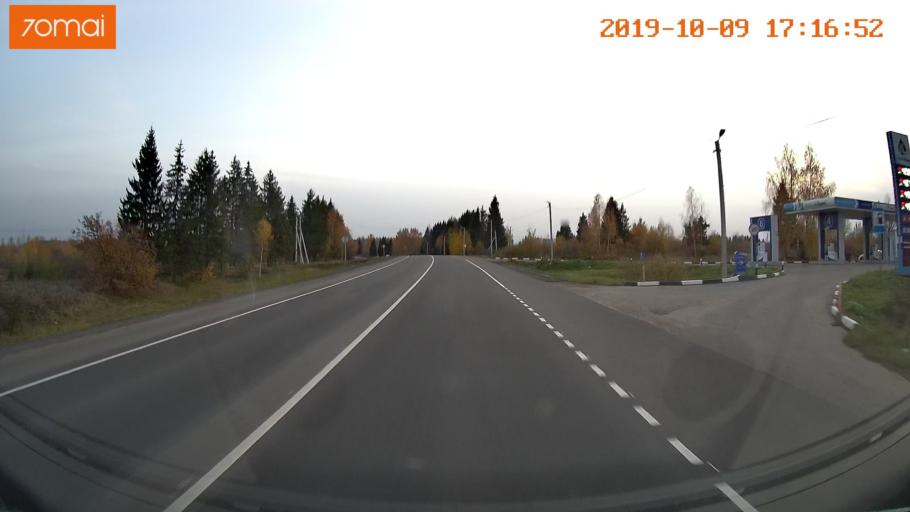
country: RU
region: Ivanovo
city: Furmanov
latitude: 57.2834
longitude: 41.1604
